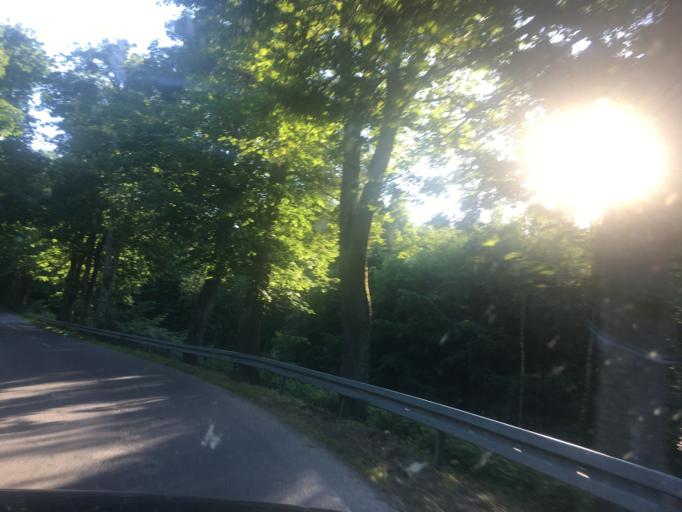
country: PL
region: Warmian-Masurian Voivodeship
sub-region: Powiat ostrodzki
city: Gierzwald
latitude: 53.6249
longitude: 20.0392
